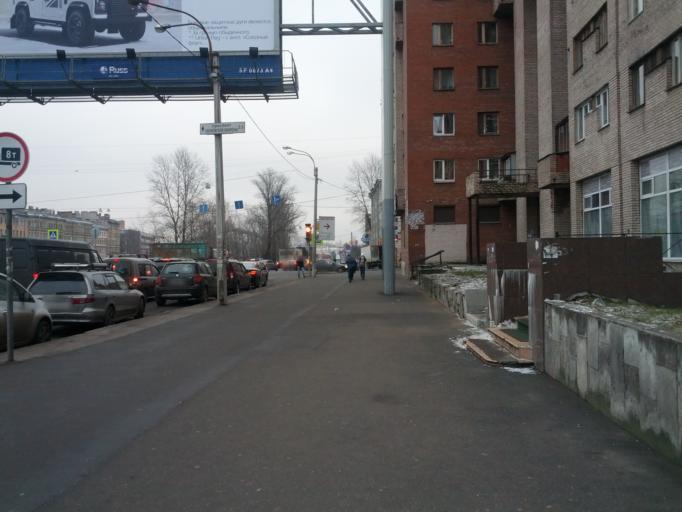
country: RU
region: St.-Petersburg
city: Centralniy
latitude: 59.9143
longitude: 30.3537
